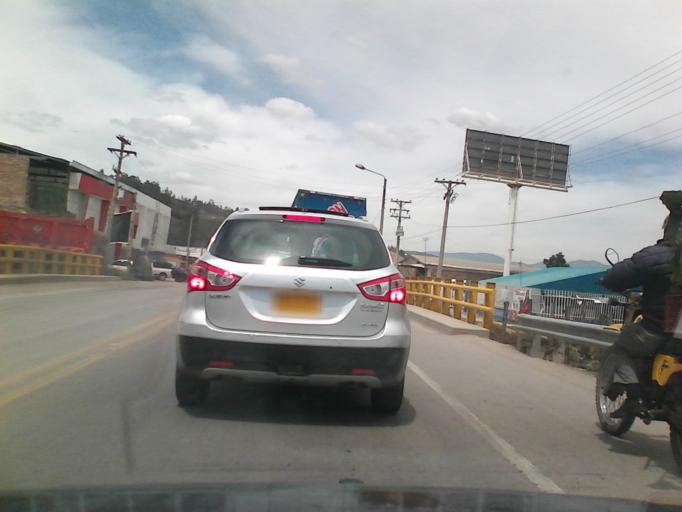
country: CO
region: Boyaca
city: Sogamoso
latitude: 5.7257
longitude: -72.9449
